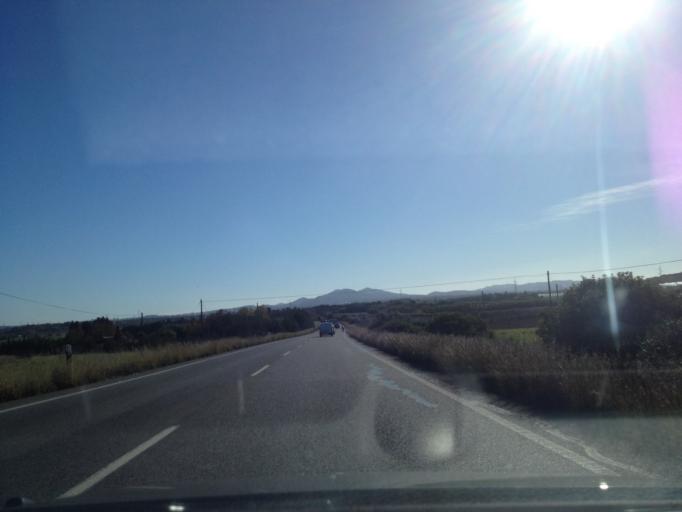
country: ES
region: Balearic Islands
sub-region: Illes Balears
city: Petra
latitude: 39.5921
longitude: 3.1375
